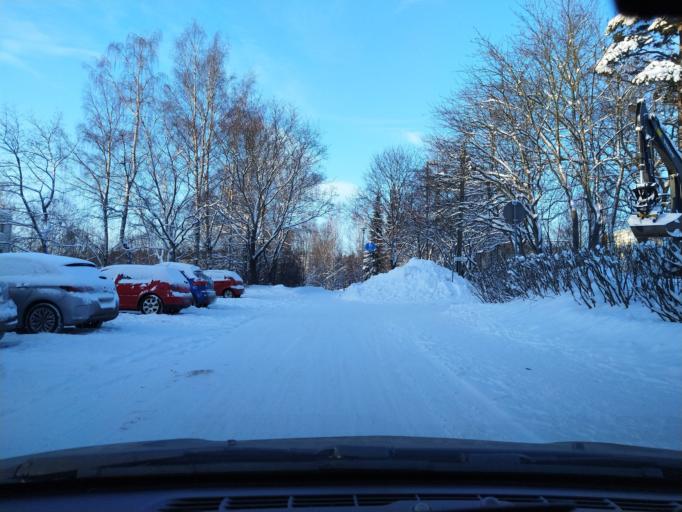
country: FI
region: Uusimaa
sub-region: Helsinki
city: Vantaa
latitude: 60.3139
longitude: 25.0273
